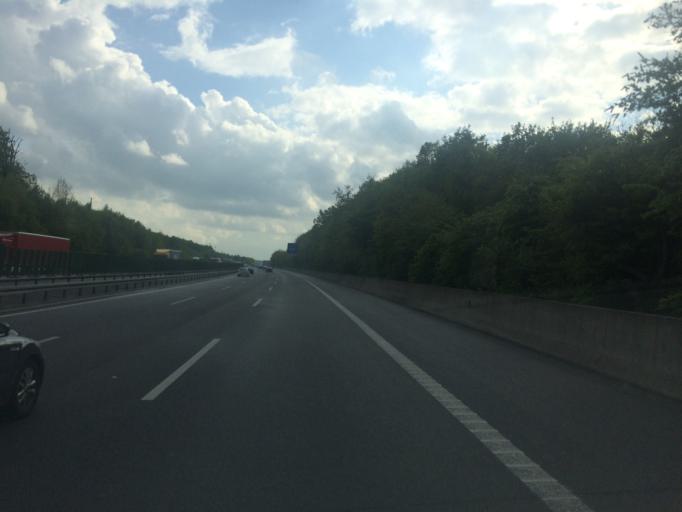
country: DE
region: Lower Saxony
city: Pohle
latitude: 52.2657
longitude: 9.3165
